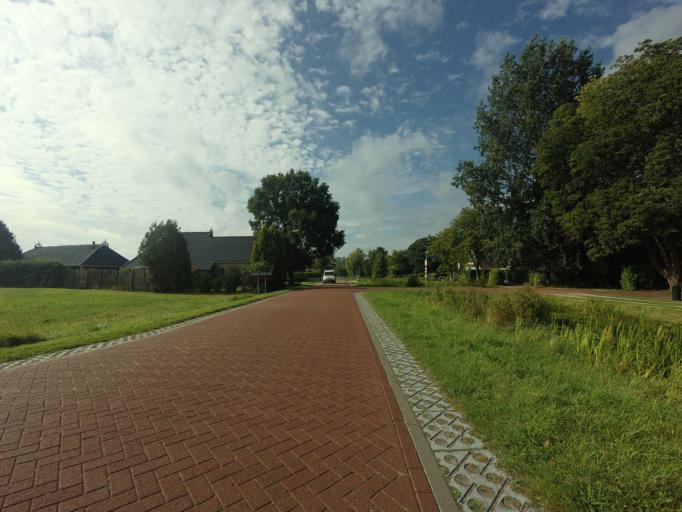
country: NL
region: Friesland
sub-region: Gemeente Heerenveen
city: Jubbega
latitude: 52.9907
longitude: 6.1039
